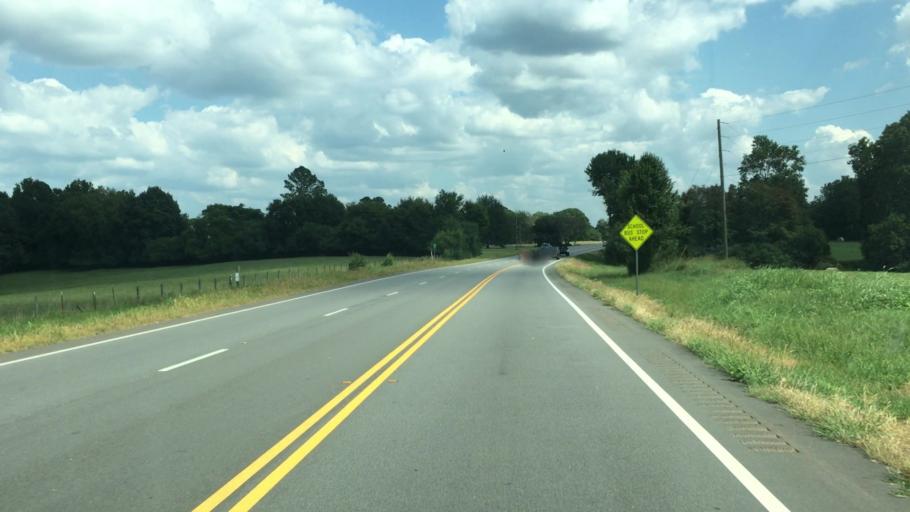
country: US
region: Georgia
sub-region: Putnam County
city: Jefferson
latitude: 33.4718
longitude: -83.4212
